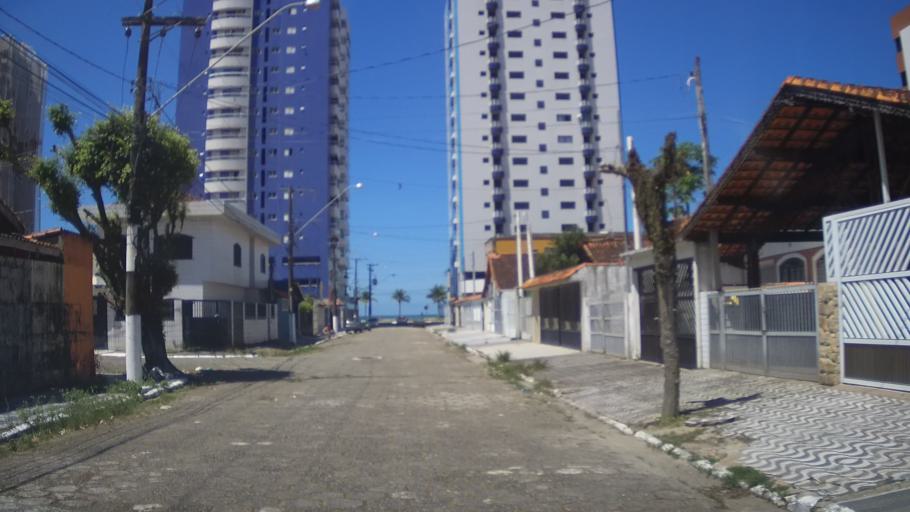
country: BR
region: Sao Paulo
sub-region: Mongagua
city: Mongagua
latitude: -24.0468
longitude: -46.5185
